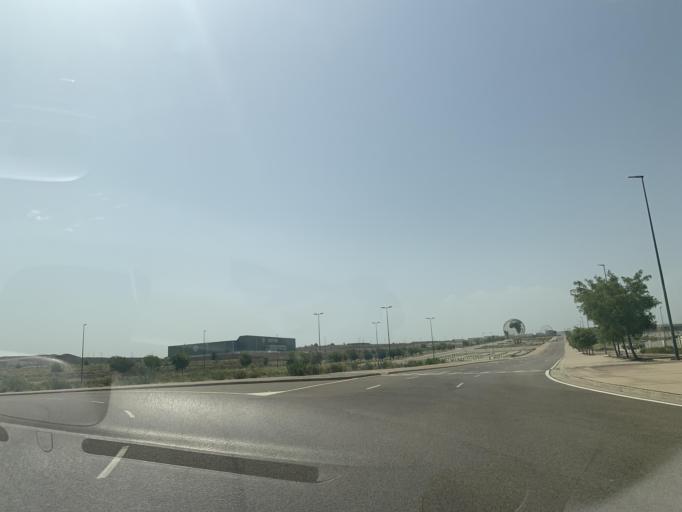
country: ES
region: Aragon
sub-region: Provincia de Zaragoza
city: Zaragoza
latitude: 41.5826
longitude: -0.8420
